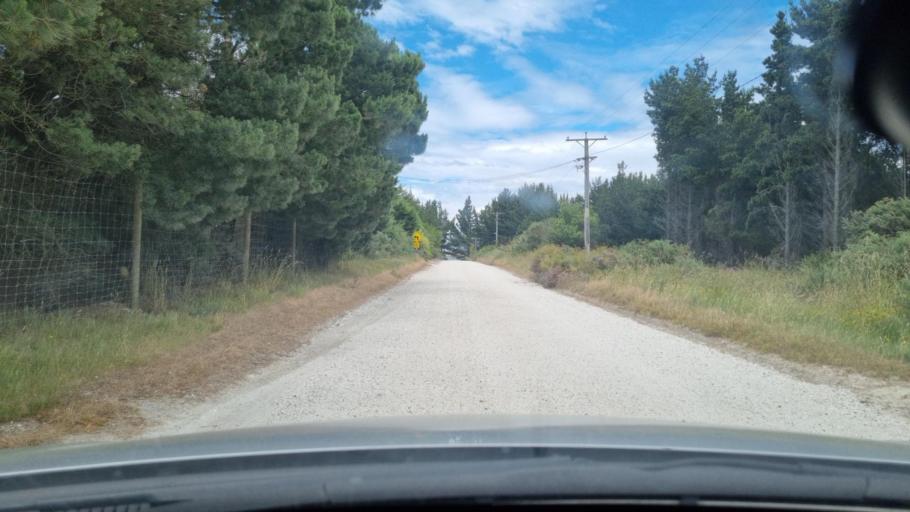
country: NZ
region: Southland
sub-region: Invercargill City
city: Bluff
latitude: -46.5581
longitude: 168.4335
